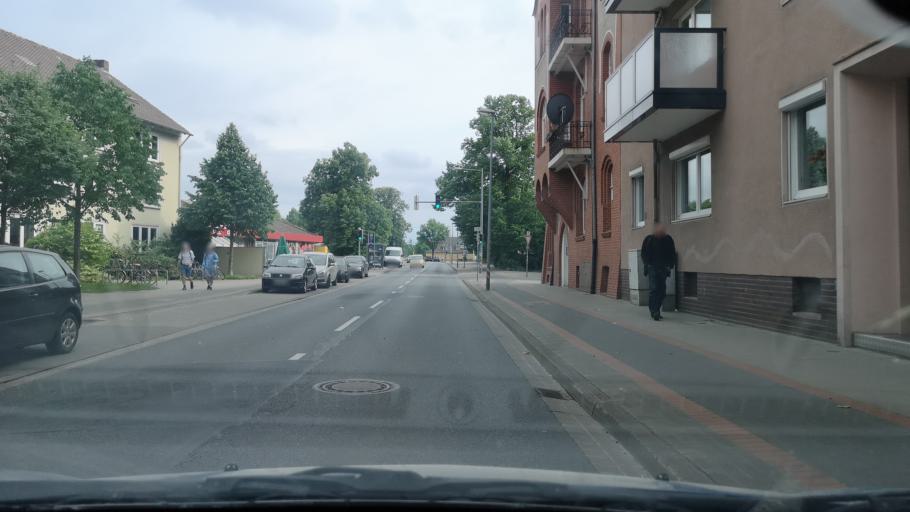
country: DE
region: Lower Saxony
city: Hannover
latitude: 52.3944
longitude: 9.6933
